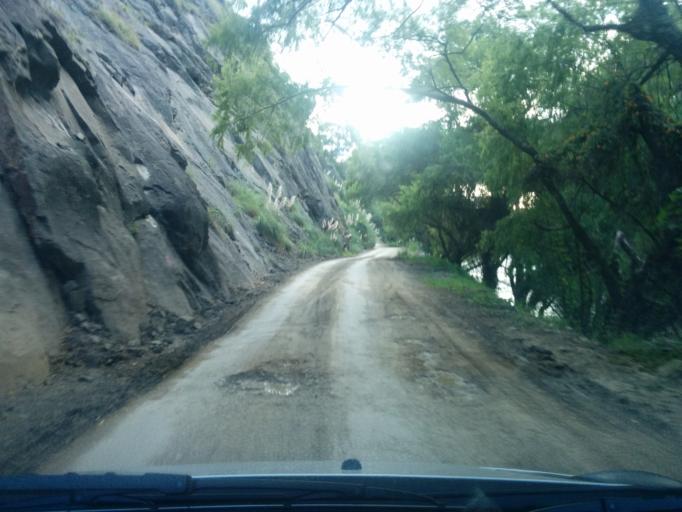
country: EC
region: Azuay
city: Cuenca
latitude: -2.8868
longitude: -78.9514
